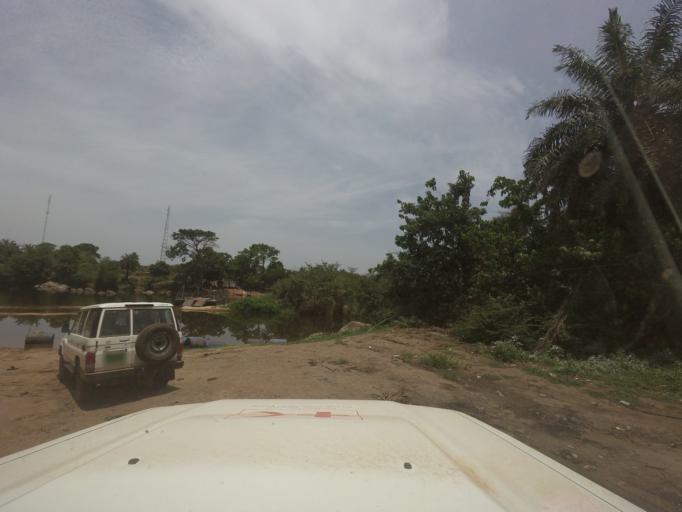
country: GN
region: Nzerekore
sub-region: Prefecture de Guekedou
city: Gueckedou
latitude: 8.5000
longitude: -10.3314
